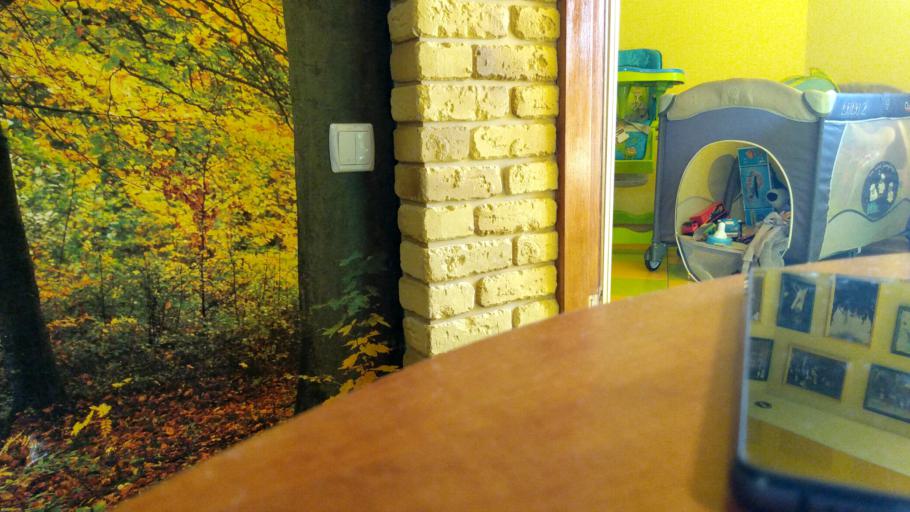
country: RU
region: Tverskaya
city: Likhoslavl'
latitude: 57.2027
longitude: 35.5137
